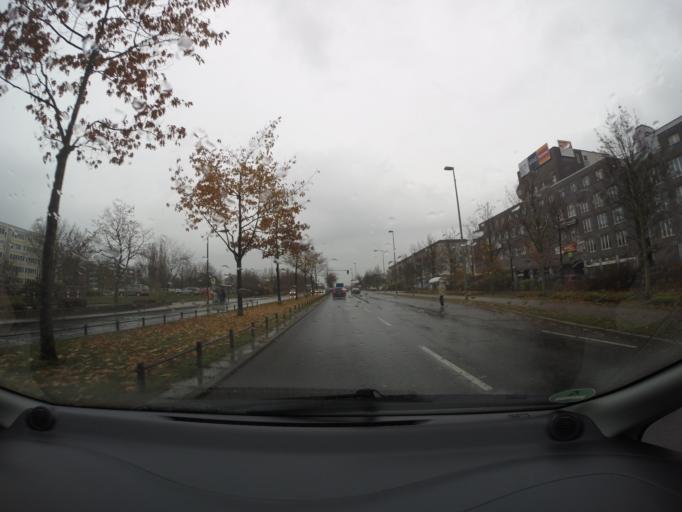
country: DE
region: Berlin
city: Falkenberg
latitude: 52.5467
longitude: 13.5375
